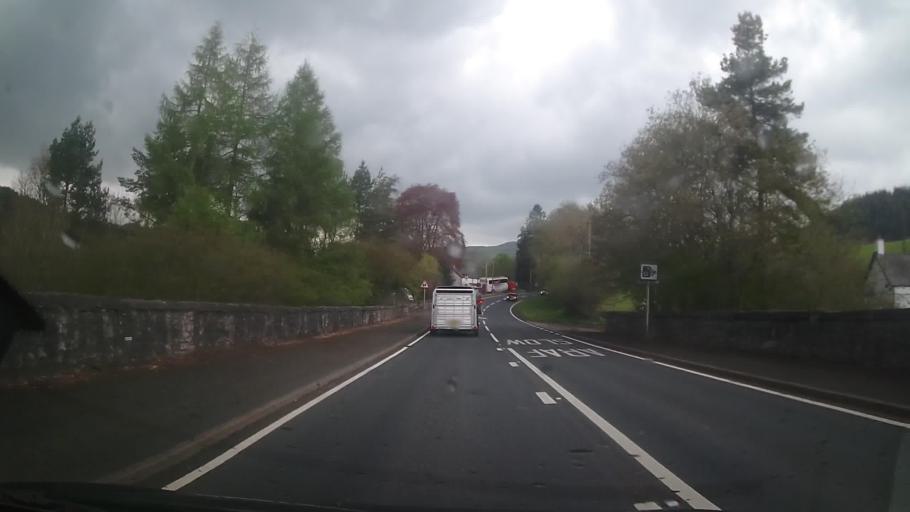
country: GB
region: Wales
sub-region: Denbighshire
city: Llandrillo
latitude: 52.9874
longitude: -3.4630
